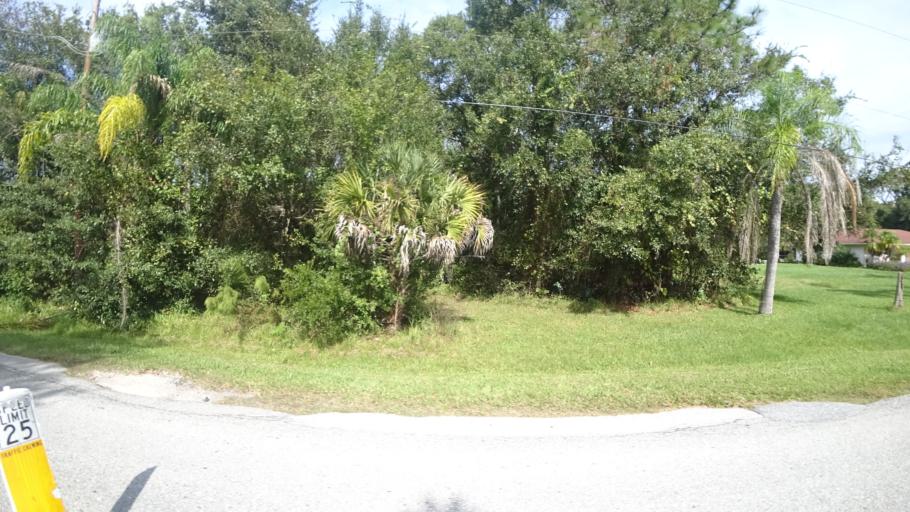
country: US
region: Florida
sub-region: Sarasota County
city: North Sarasota
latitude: 27.3870
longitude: -82.5118
